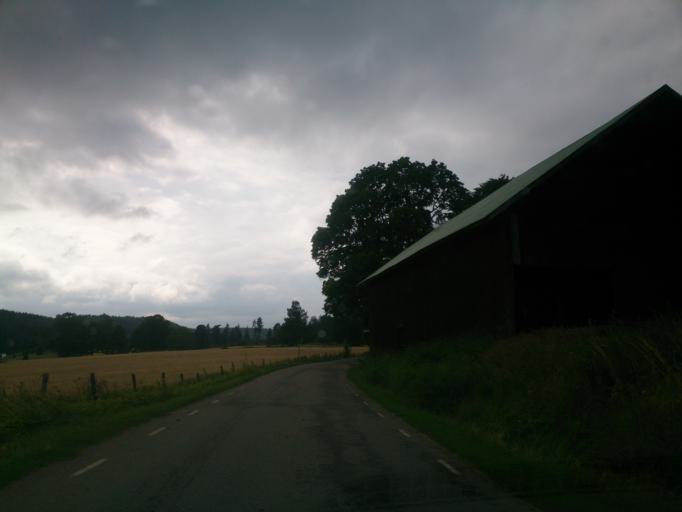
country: SE
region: OEstergoetland
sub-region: Atvidabergs Kommun
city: Atvidaberg
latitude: 58.2761
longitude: 16.1175
